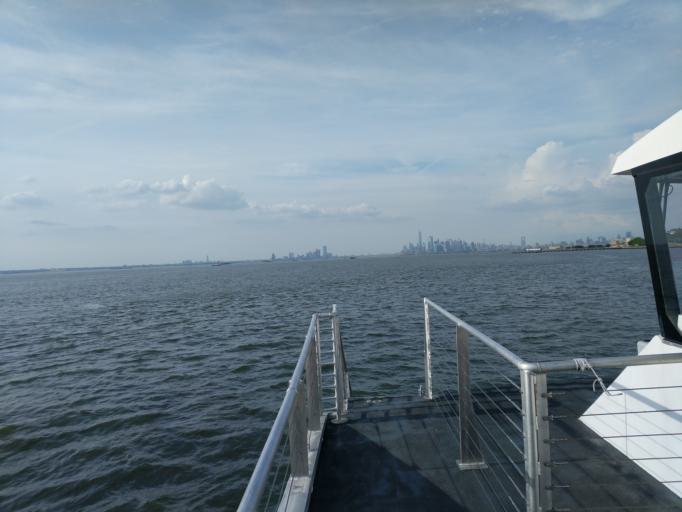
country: US
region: New York
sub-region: Kings County
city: Bensonhurst
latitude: 40.6317
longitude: -74.0438
